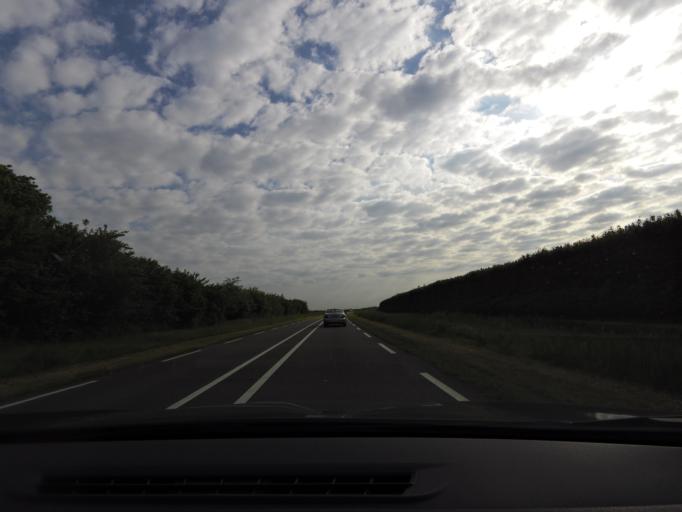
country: NL
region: Zeeland
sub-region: Schouwen-Duiveland
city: Haamstede
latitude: 51.7014
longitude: 3.7501
